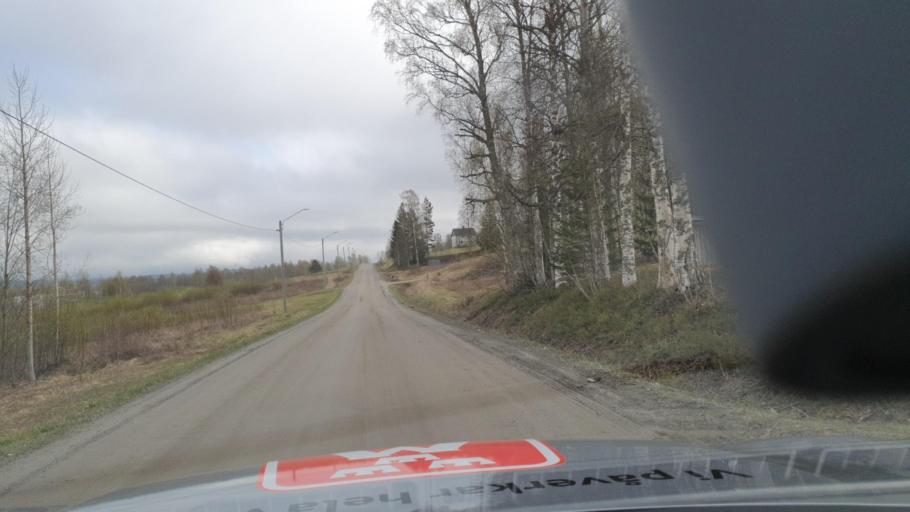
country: SE
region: Vaesterbotten
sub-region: Bjurholms Kommun
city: Bjurholm
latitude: 63.6668
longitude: 19.0110
